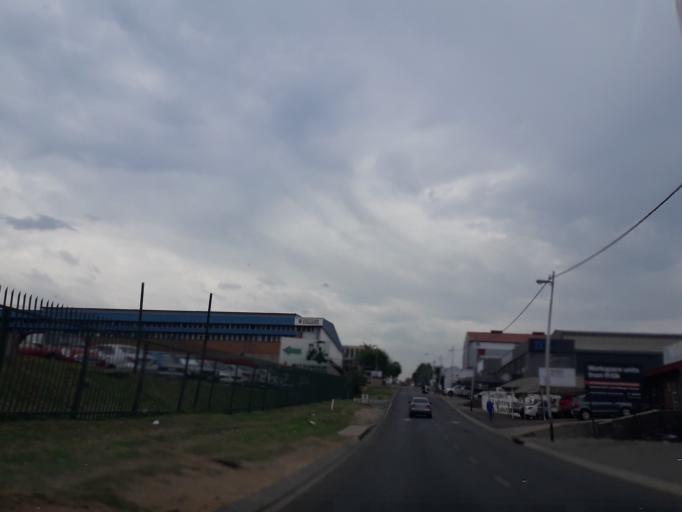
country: ZA
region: Gauteng
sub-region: City of Johannesburg Metropolitan Municipality
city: Modderfontein
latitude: -26.1060
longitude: 28.0817
